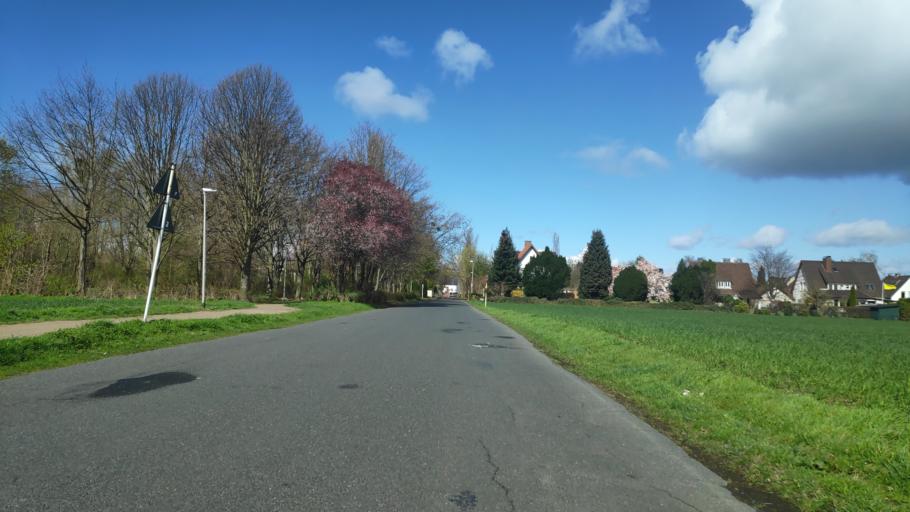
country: DE
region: North Rhine-Westphalia
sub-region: Regierungsbezirk Detmold
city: Minden
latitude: 52.2942
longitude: 8.8952
